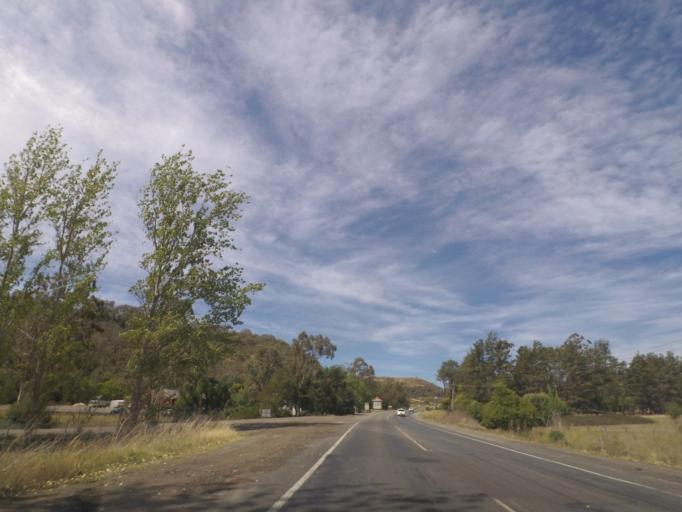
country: AU
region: New South Wales
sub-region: Wollondilly
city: Picton
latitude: -34.1641
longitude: 150.6345
